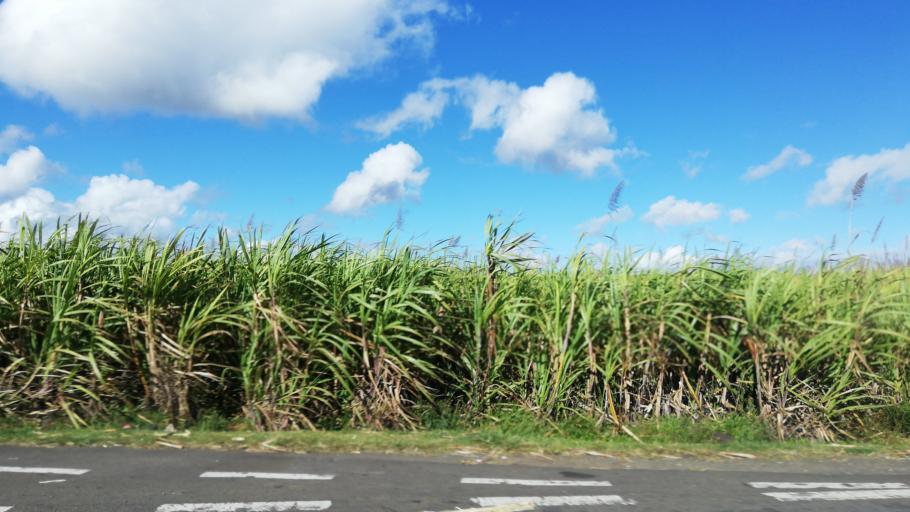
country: MU
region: Moka
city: Quartier Militaire
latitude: -20.2449
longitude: 57.5888
